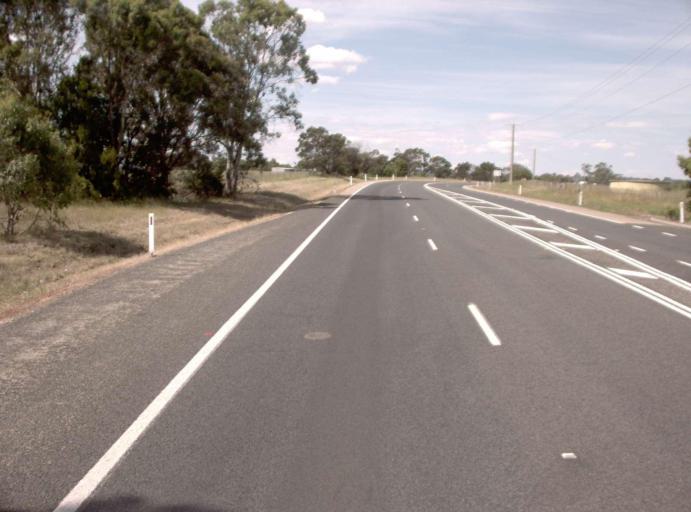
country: AU
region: Victoria
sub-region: East Gippsland
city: Bairnsdale
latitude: -37.8232
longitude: 147.7206
